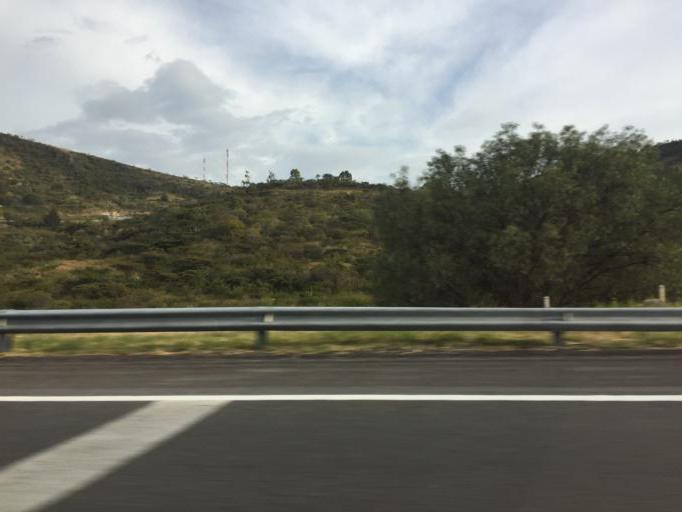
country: MX
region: Michoacan
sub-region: Cuitzeo
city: San Juan Benito Juarez (San Juan Tararameo)
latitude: 19.8937
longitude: -101.1522
